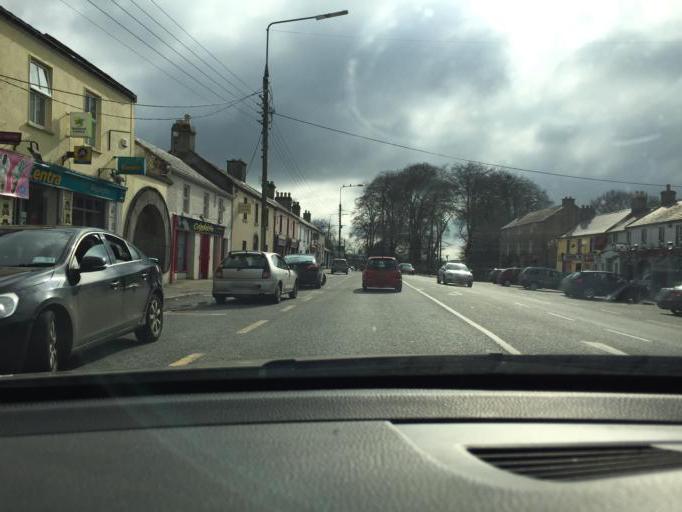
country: IE
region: Leinster
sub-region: Wicklow
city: Blessington
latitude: 53.1702
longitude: -6.5334
